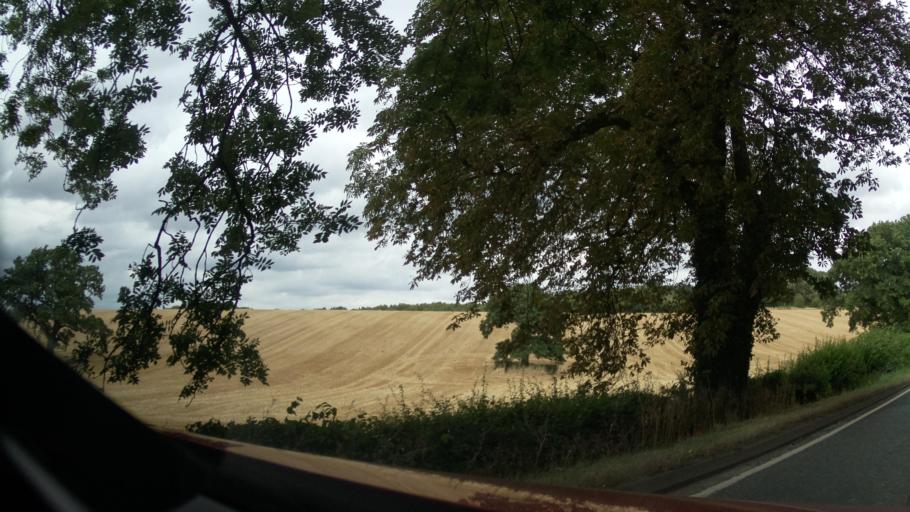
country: GB
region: England
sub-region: Leicestershire
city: Castle Donington
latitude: 52.8194
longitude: -1.3762
